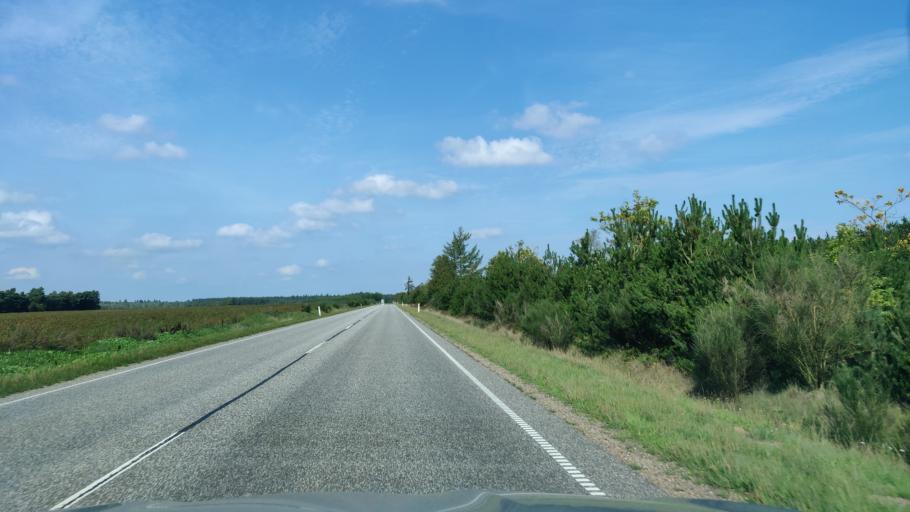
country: DK
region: Central Jutland
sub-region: Herning Kommune
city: Sunds
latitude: 56.3428
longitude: 8.9786
